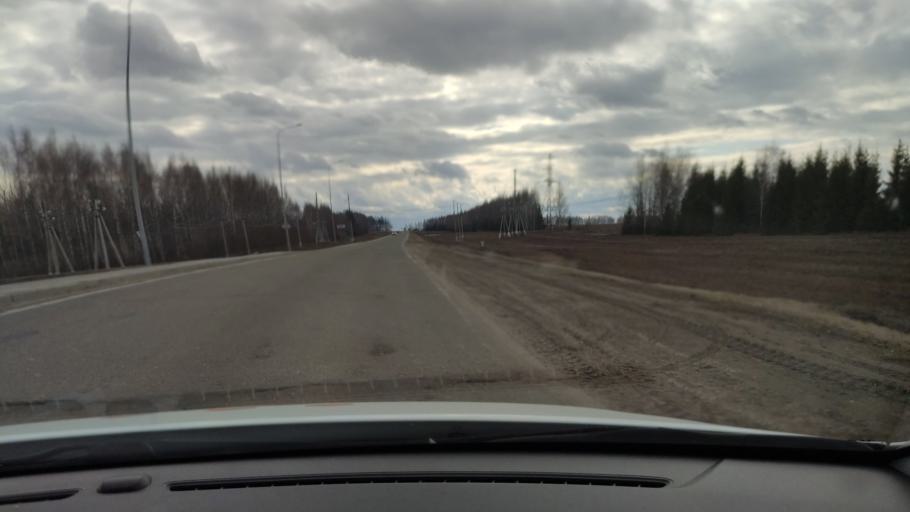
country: RU
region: Tatarstan
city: Vysokaya Gora
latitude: 56.1112
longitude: 49.1836
